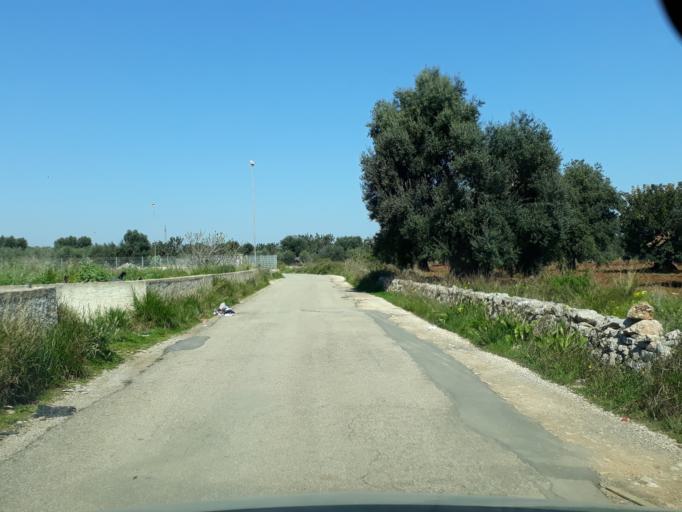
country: IT
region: Apulia
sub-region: Provincia di Brindisi
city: Fasano
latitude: 40.8284
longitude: 17.3816
